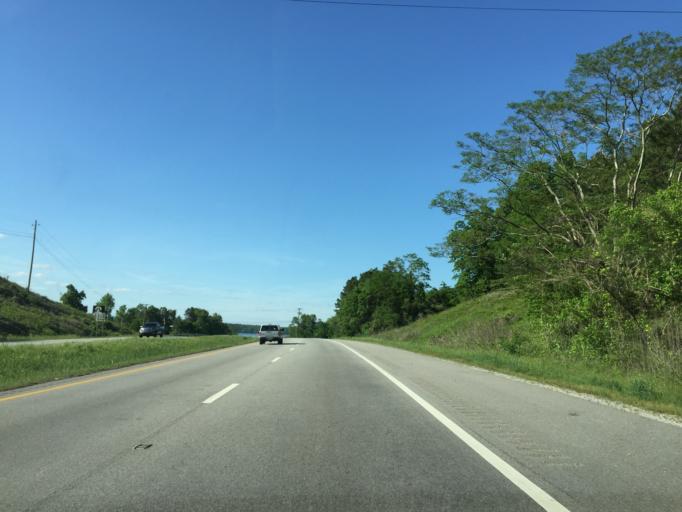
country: US
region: Tennessee
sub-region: Hamilton County
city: Harrison
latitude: 35.1329
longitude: -85.1220
